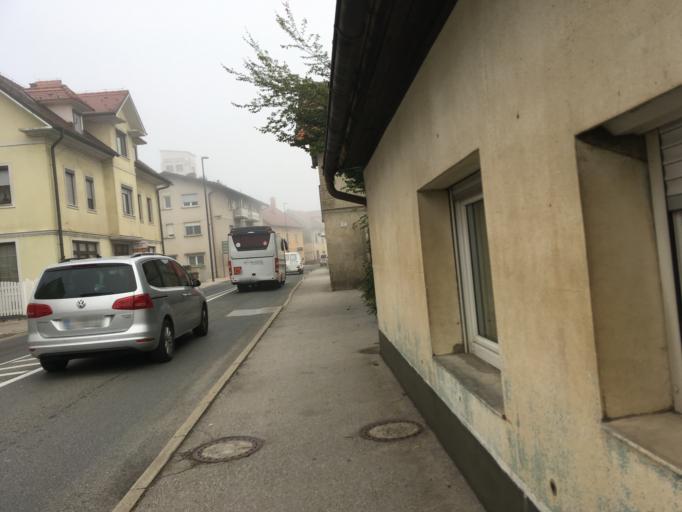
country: SI
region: Menges
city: Menges
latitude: 46.1659
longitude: 14.5720
